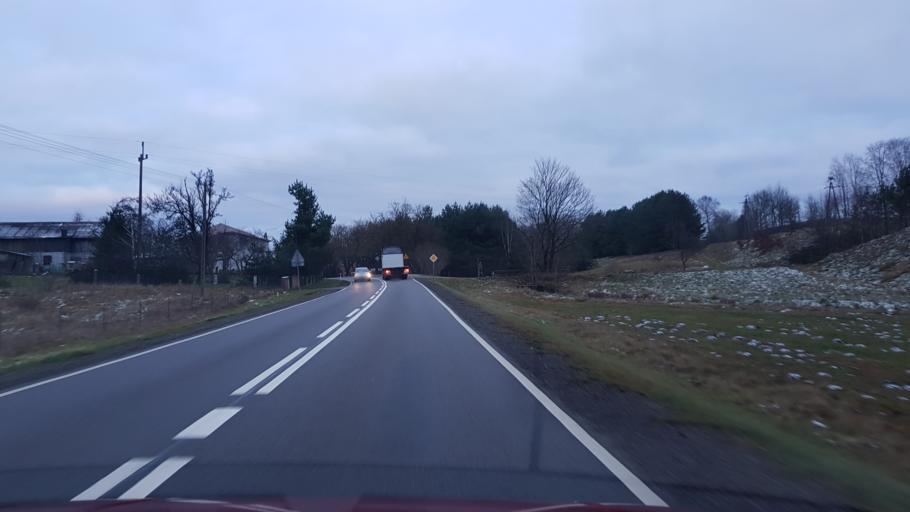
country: PL
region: Pomeranian Voivodeship
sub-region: Powiat bytowski
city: Tuchomie
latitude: 54.0414
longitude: 17.2022
